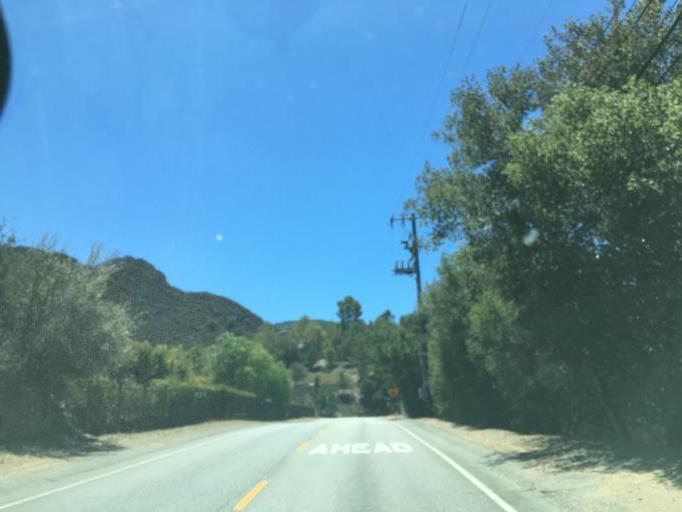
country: US
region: California
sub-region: Los Angeles County
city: Agoura Hills
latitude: 34.1149
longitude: -118.7852
